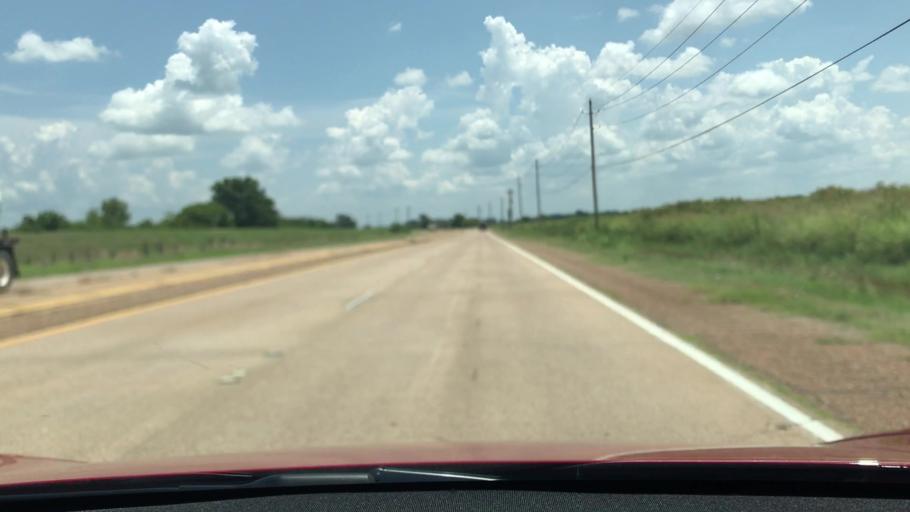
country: US
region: Louisiana
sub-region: Bossier Parish
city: Bossier City
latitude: 32.3929
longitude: -93.6862
